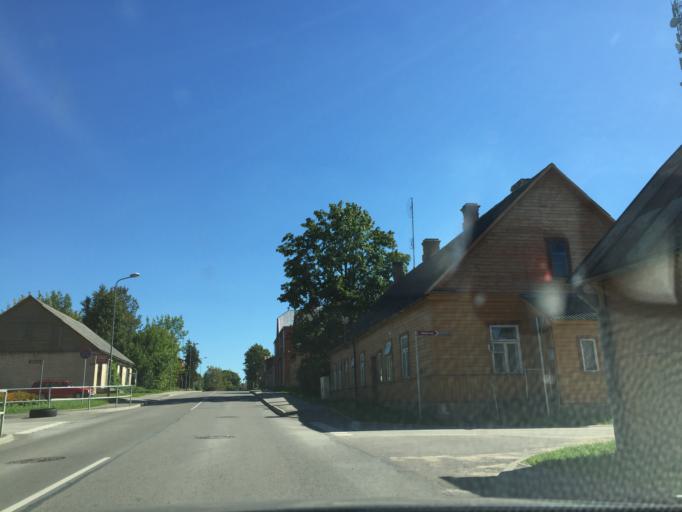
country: LV
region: Akniste
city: Akniste
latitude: 56.1604
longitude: 25.7503
